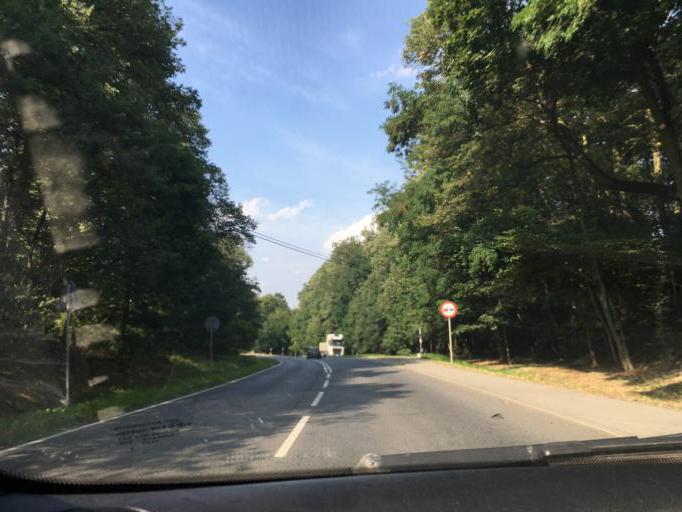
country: PL
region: Opole Voivodeship
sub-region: Powiat prudnicki
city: Laka Prudnicka
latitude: 50.4022
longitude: 17.5095
